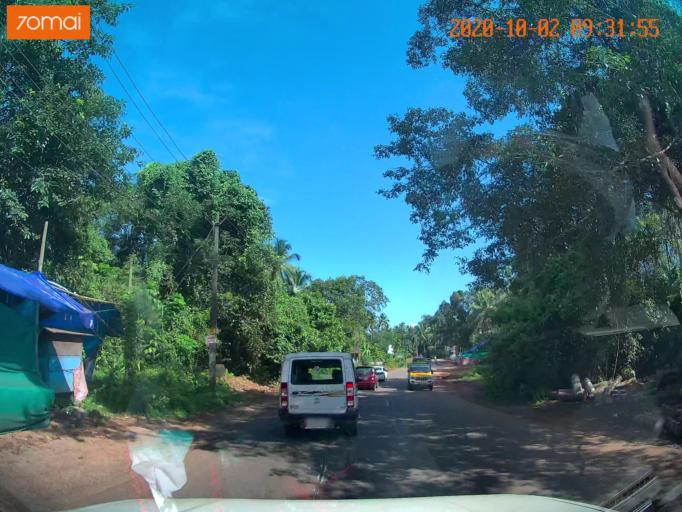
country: IN
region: Kerala
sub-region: Kozhikode
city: Nadapuram
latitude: 11.6250
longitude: 75.7574
